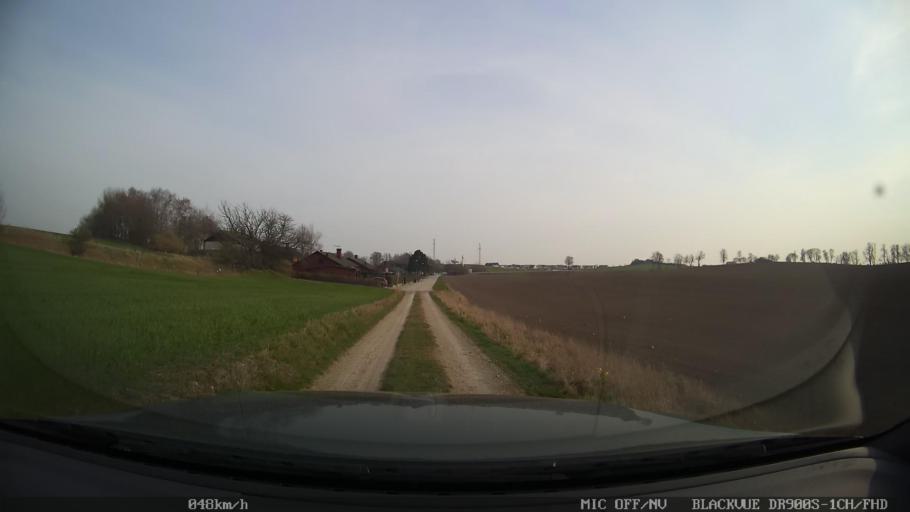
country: SE
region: Skane
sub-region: Ystads Kommun
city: Ystad
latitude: 55.4526
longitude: 13.7940
